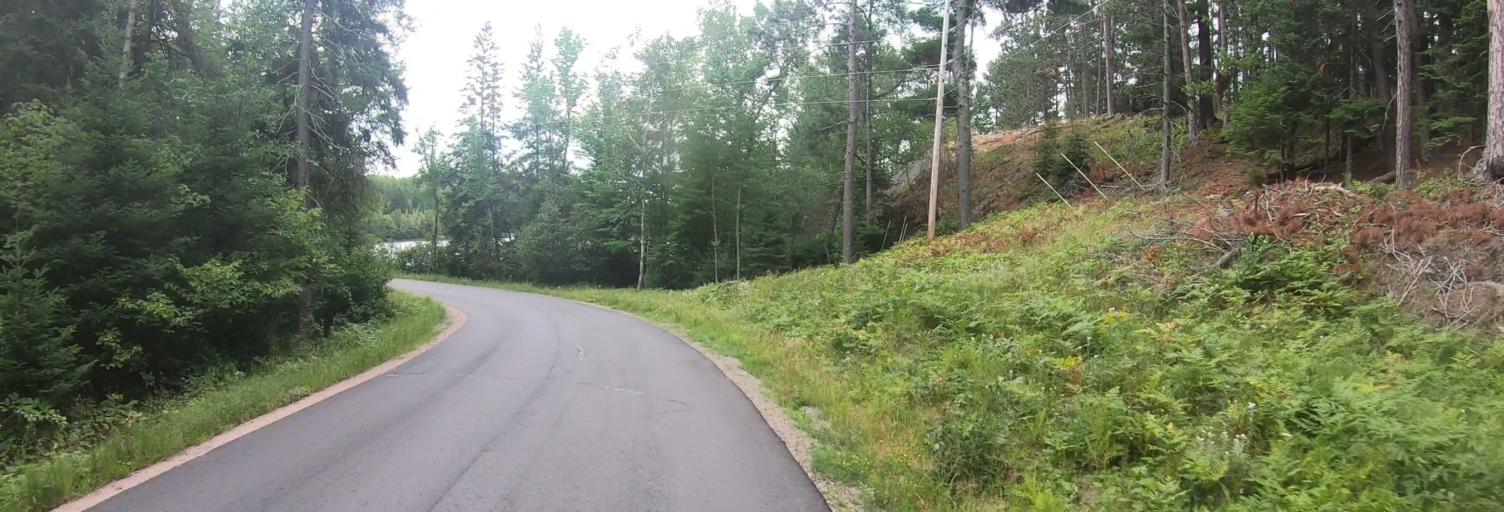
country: US
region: Minnesota
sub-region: Saint Louis County
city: Mountain Iron
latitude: 47.9532
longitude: -92.6247
